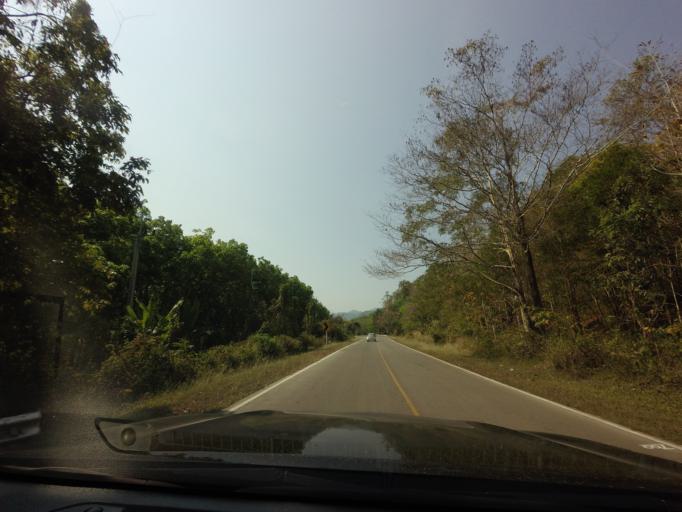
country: TH
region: Kanchanaburi
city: Thong Pha Phum
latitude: 14.6725
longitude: 98.5289
